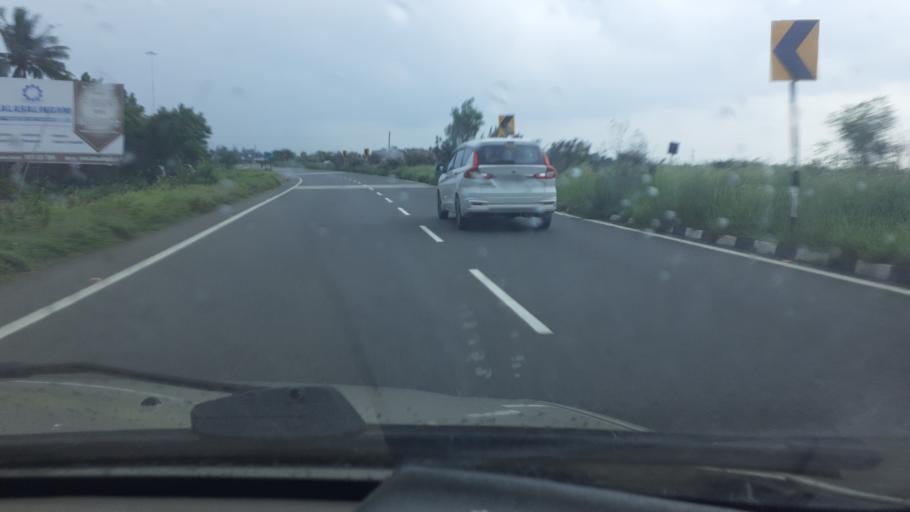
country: IN
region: Tamil Nadu
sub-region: Virudhunagar
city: Virudunagar
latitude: 9.6478
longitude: 77.9639
